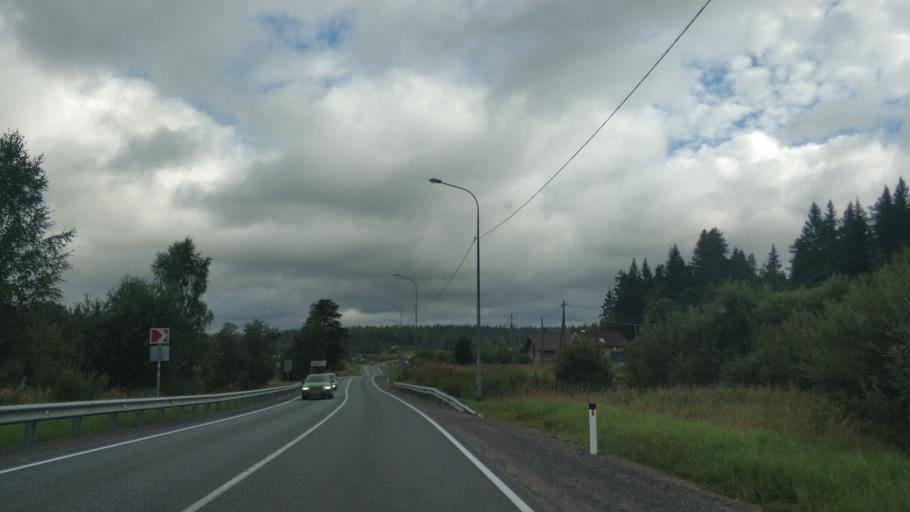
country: RU
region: Republic of Karelia
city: Khelyulya
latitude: 61.7557
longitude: 30.6566
